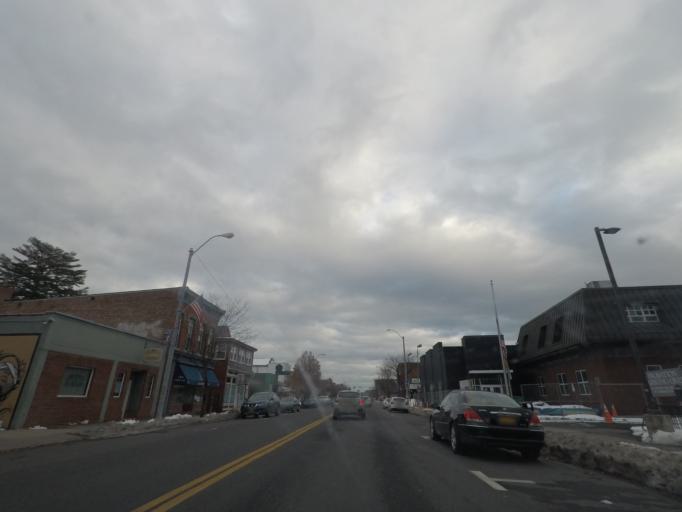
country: US
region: New York
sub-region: Ulster County
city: Kingston
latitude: 41.9318
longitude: -74.0105
